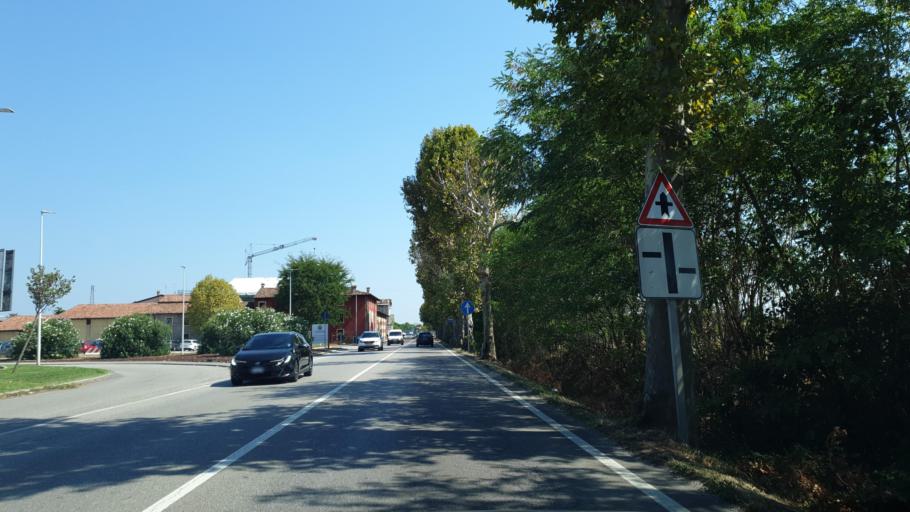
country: IT
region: Veneto
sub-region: Provincia di Verona
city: Lugagnano
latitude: 45.4464
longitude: 10.8814
